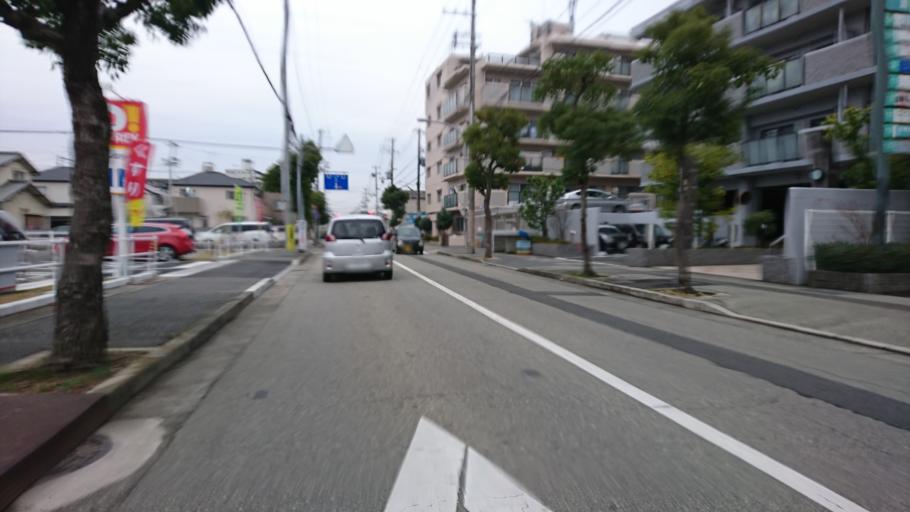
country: JP
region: Hyogo
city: Kakogawacho-honmachi
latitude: 34.7679
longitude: 134.8234
